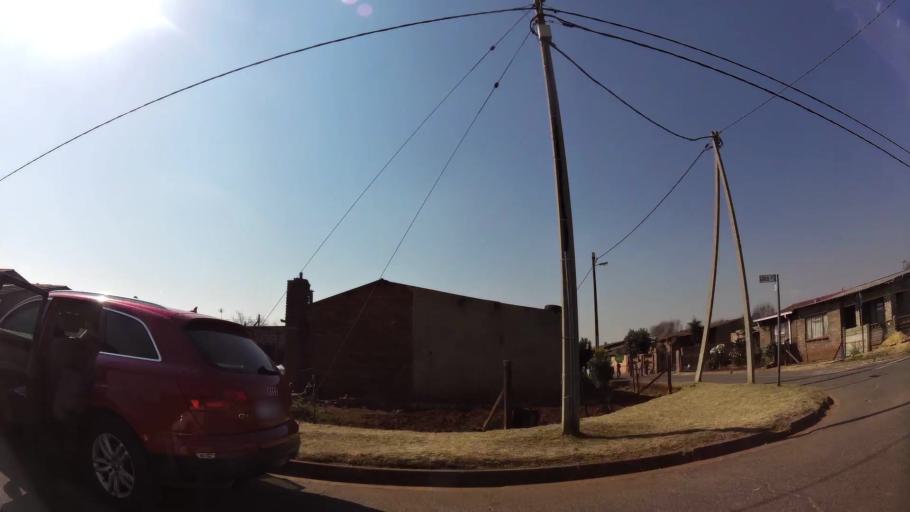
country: ZA
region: Gauteng
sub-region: Ekurhuleni Metropolitan Municipality
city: Boksburg
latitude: -26.2168
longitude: 28.2944
